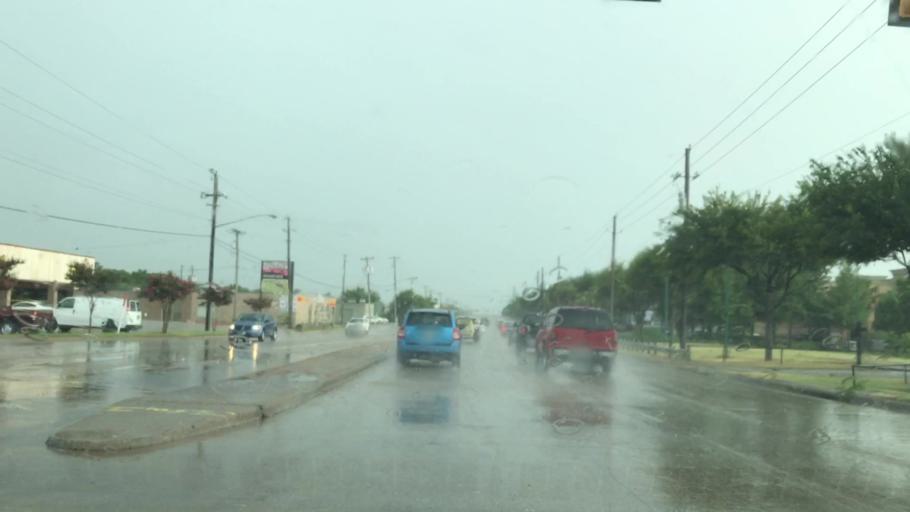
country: US
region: Texas
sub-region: Dallas County
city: Richardson
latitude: 32.8944
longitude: -96.7004
